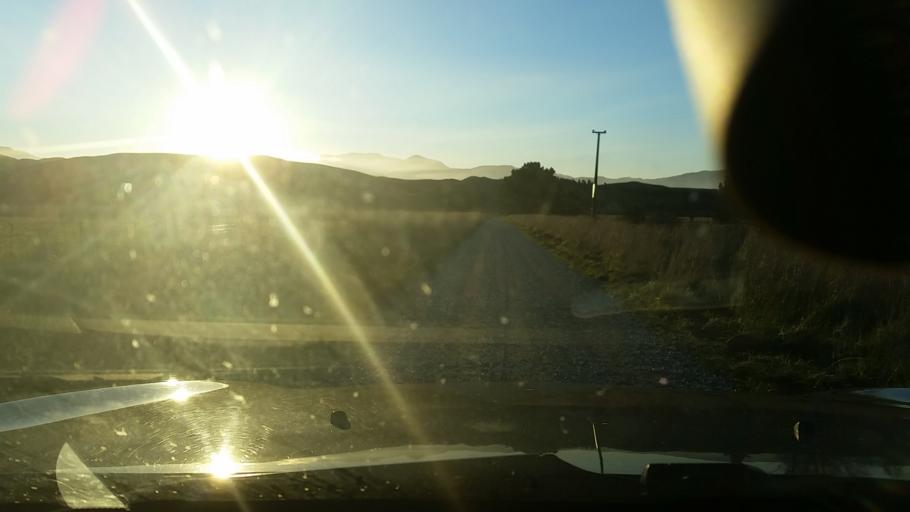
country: NZ
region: Marlborough
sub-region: Marlborough District
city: Blenheim
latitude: -41.7366
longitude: 174.0411
